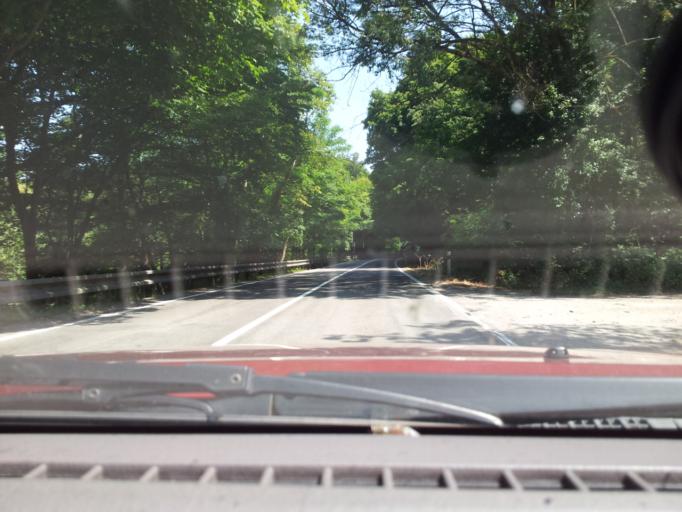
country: SK
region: Trnavsky
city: Smolenice
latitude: 48.5518
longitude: 17.4520
